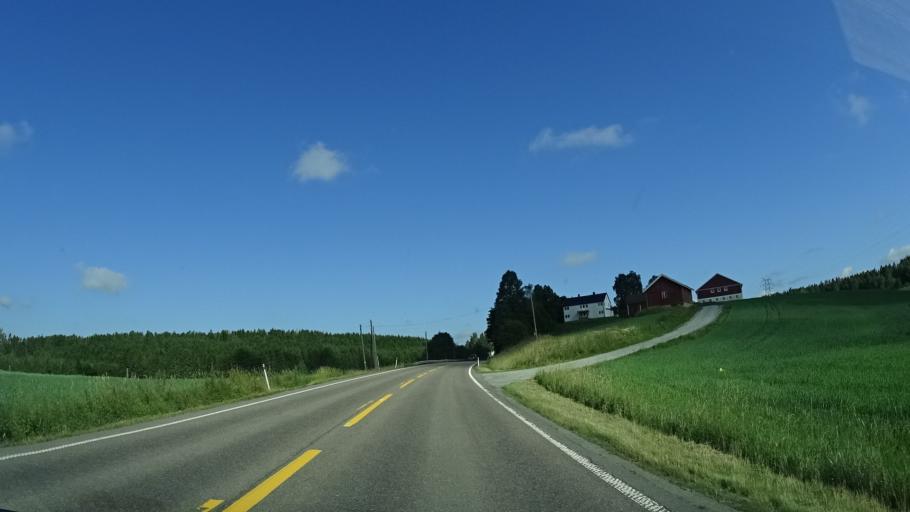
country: NO
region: Ostfold
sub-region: Hobol
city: Elvestad
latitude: 59.6591
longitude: 10.9114
